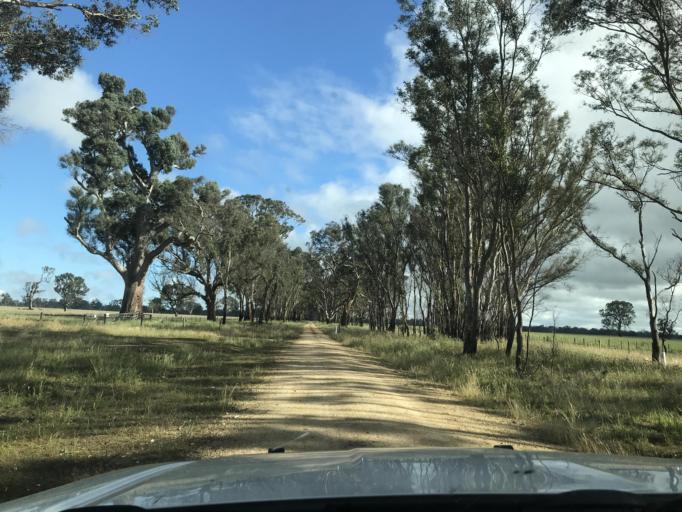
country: AU
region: South Australia
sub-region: Wattle Range
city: Penola
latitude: -37.2099
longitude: 141.1299
